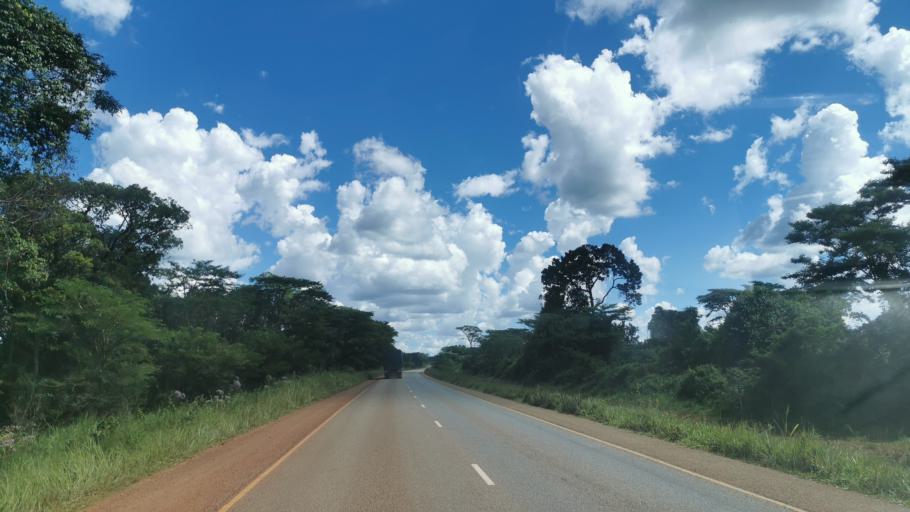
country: TZ
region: Geita
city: Uyovu
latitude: -3.0516
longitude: 31.2553
